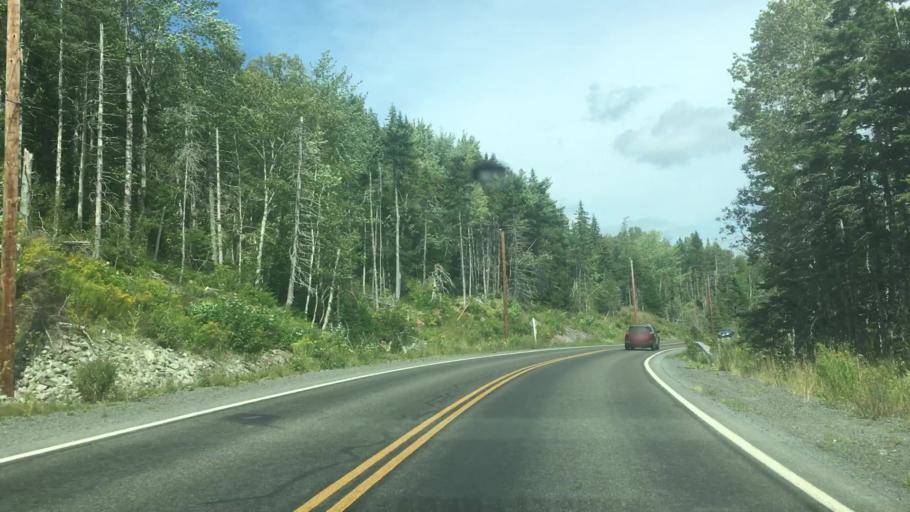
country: CA
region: Nova Scotia
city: Sydney Mines
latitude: 46.2077
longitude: -60.6228
